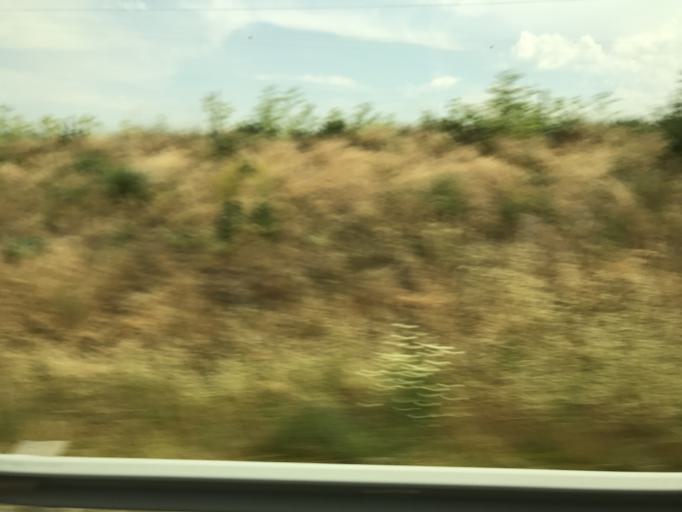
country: ES
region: Madrid
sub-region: Provincia de Madrid
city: Buitrago del Lozoya
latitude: 40.9870
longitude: -3.6412
